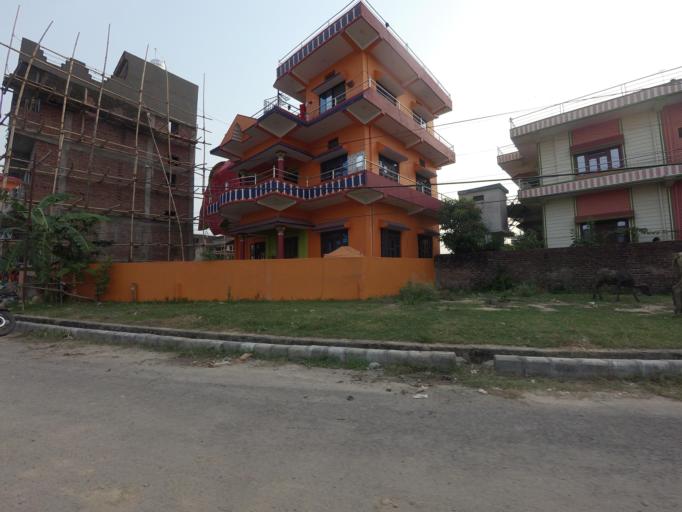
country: NP
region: Western Region
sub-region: Lumbini Zone
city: Bhairahawa
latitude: 27.5138
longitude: 83.4604
